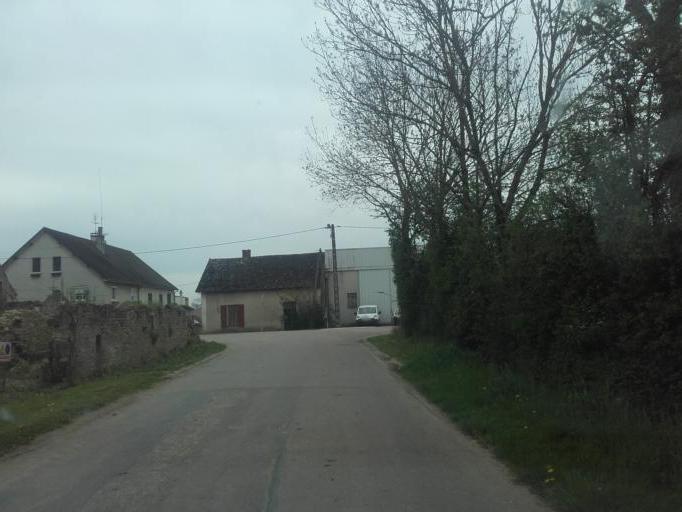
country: FR
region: Bourgogne
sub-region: Departement de la Cote-d'Or
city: Bligny-les-Beaune
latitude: 46.9804
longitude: 4.8491
